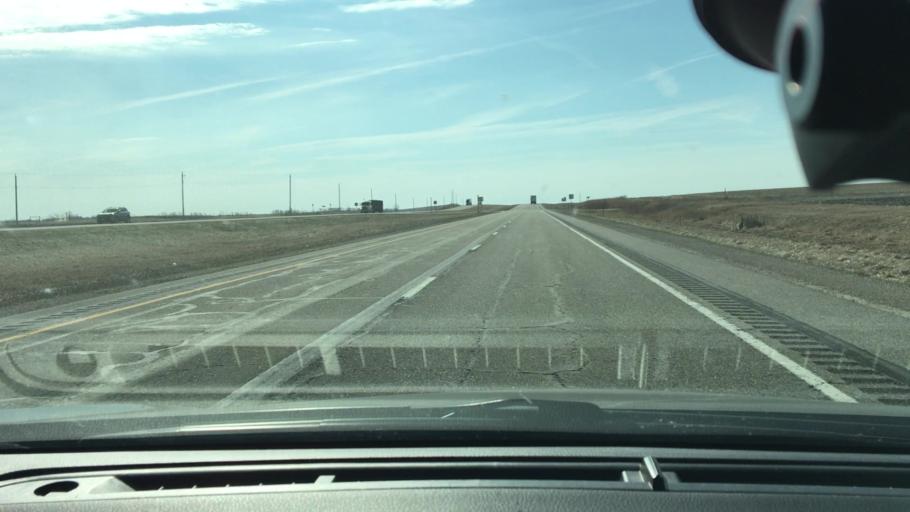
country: US
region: Iowa
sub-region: Chickasaw County
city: Nashua
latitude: 42.9916
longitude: -92.5944
